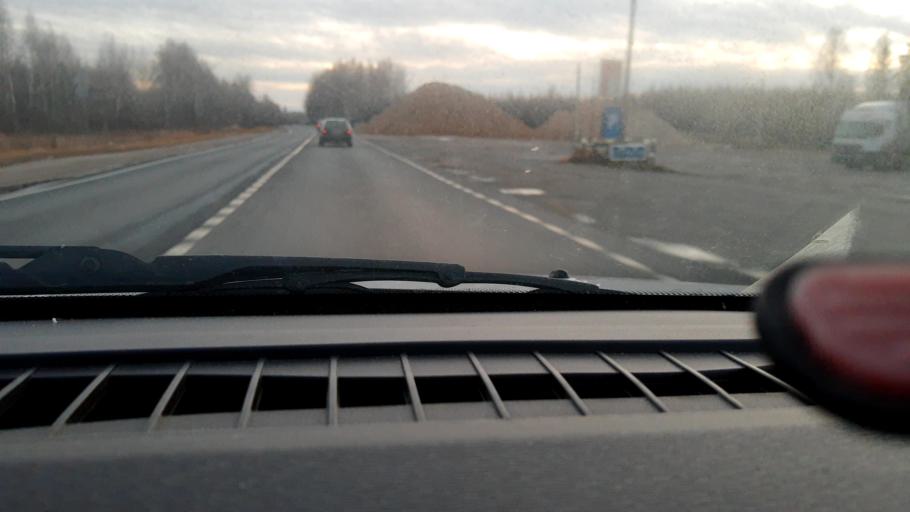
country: RU
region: Nizjnij Novgorod
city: Krasnyye Baki
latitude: 57.0811
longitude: 45.1453
